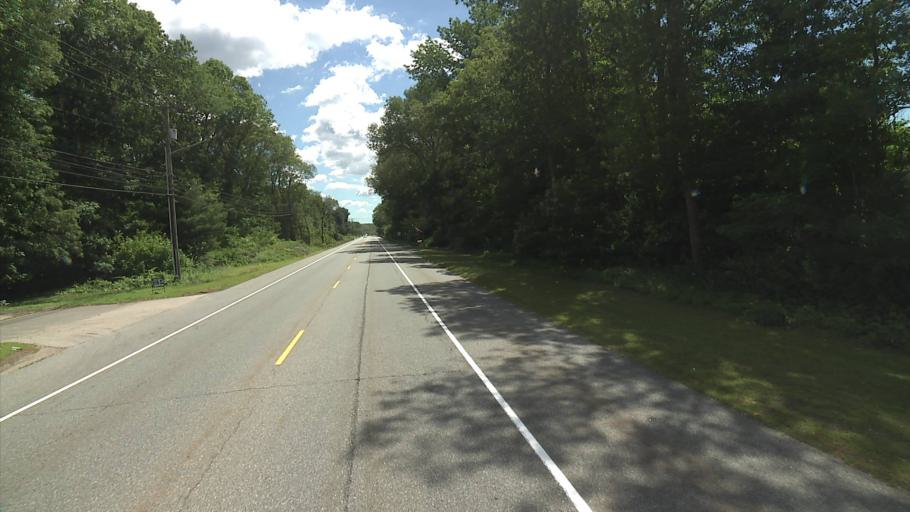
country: US
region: Connecticut
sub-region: New London County
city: Old Mystic
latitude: 41.3896
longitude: -71.9937
